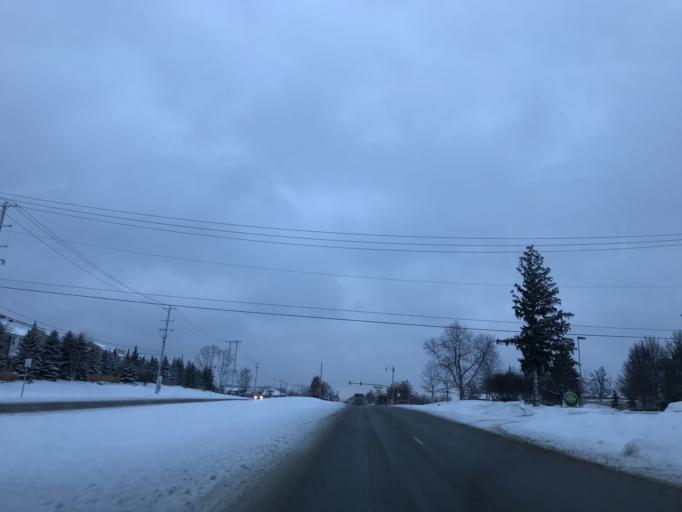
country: US
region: Michigan
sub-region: Oakland County
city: Novi
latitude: 42.4952
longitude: -83.4894
